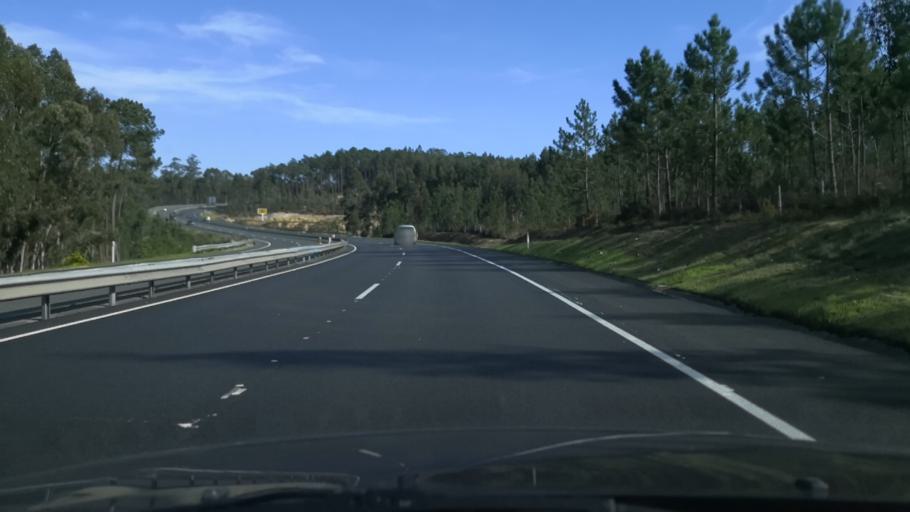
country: PT
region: Leiria
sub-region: Leiria
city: Leiria
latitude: 39.7395
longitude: -8.7627
